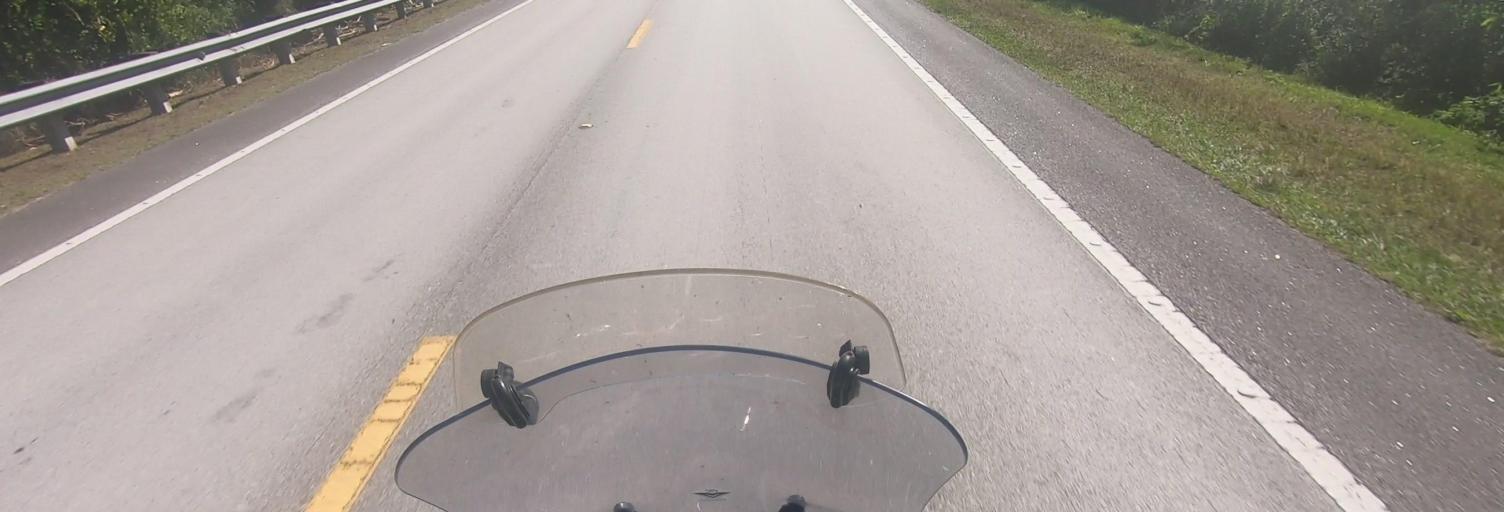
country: US
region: Florida
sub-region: Collier County
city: Marco
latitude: 25.8753
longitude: -81.2244
